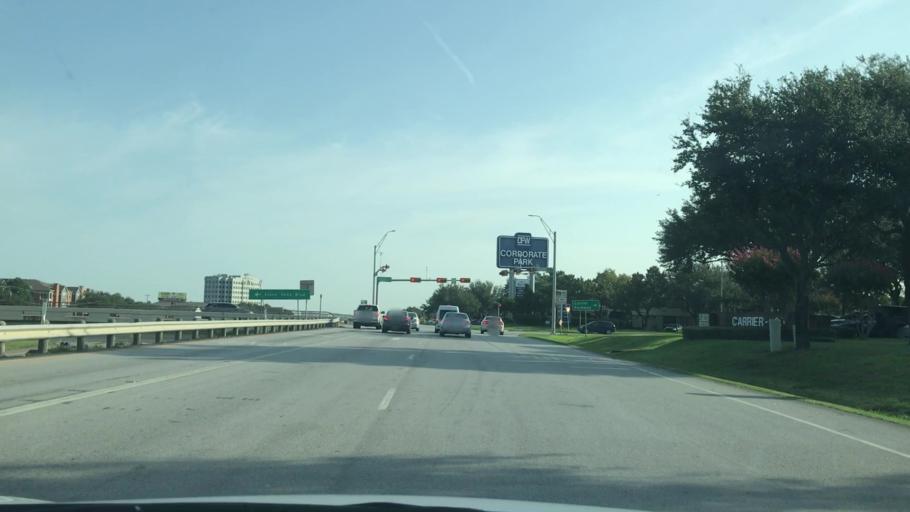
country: US
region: Texas
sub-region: Tarrant County
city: Euless
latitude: 32.7847
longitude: -97.0590
